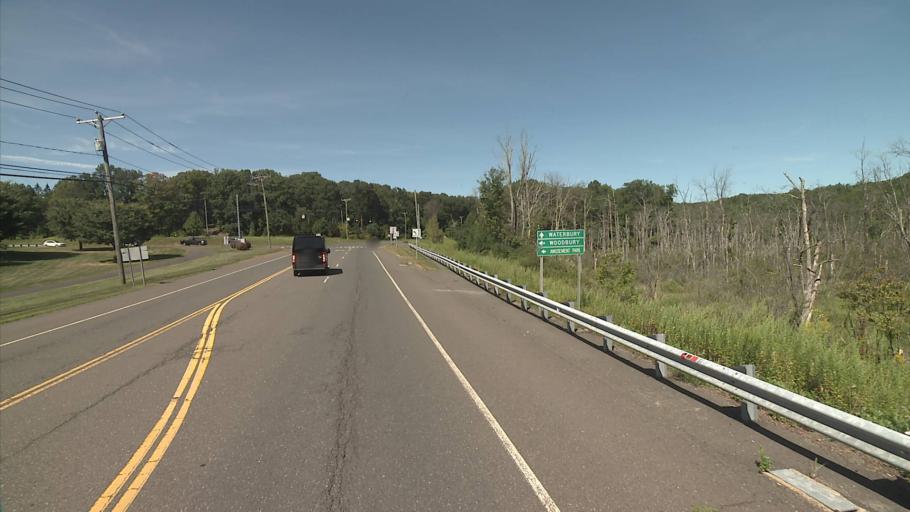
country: US
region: Connecticut
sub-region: New Haven County
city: Middlebury
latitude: 41.5207
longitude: -73.1358
